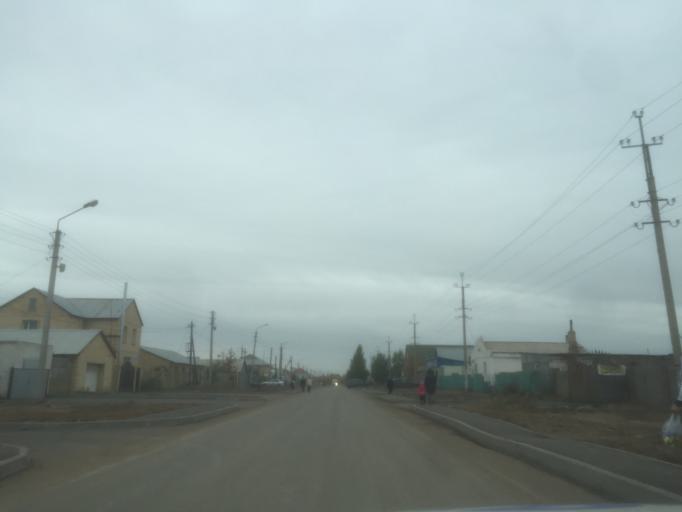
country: KZ
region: Astana Qalasy
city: Astana
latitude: 51.1956
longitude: 71.3292
